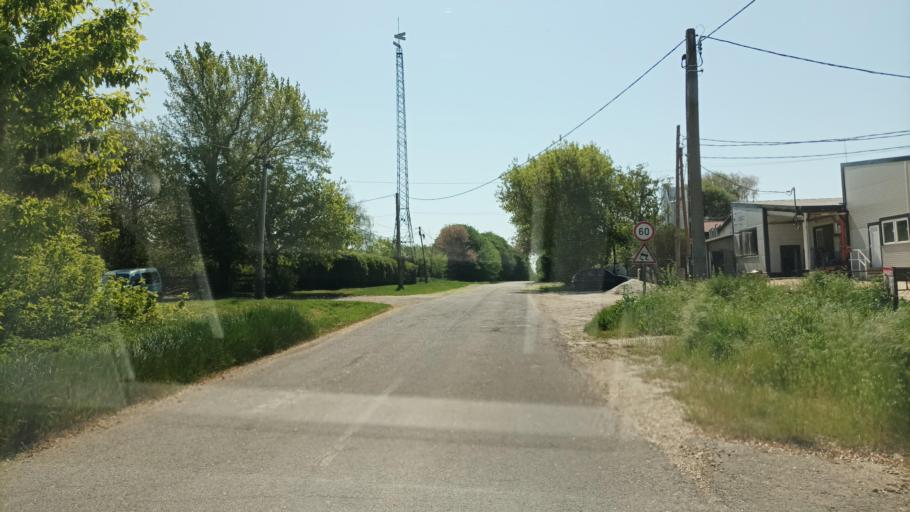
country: HU
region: Pest
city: Uri
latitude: 47.3960
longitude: 19.4937
